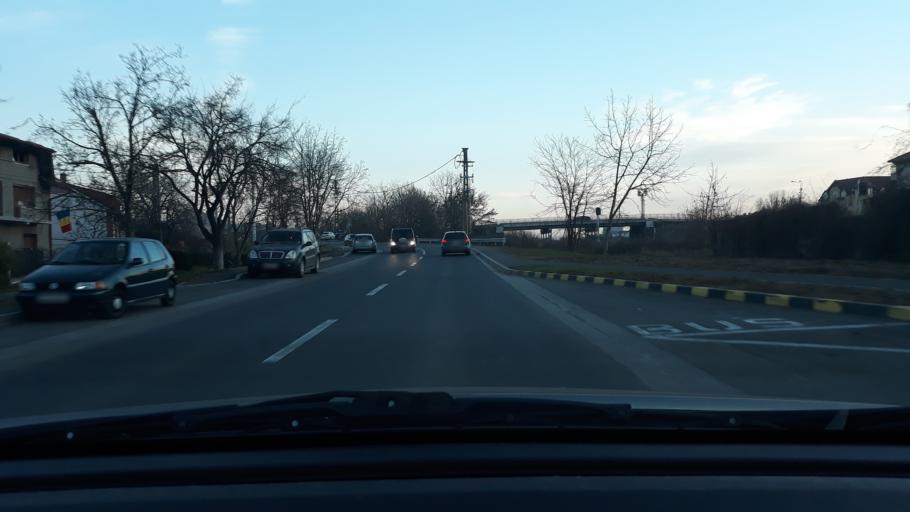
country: RO
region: Bihor
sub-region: Comuna Biharea
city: Oradea
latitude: 47.0794
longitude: 21.9295
